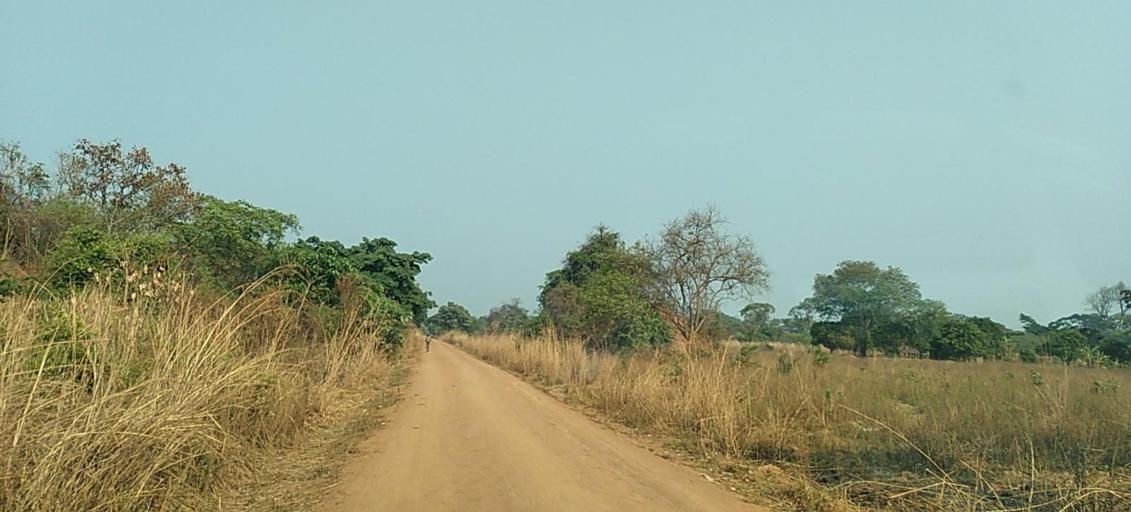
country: ZM
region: Copperbelt
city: Chingola
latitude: -12.8565
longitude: 27.5619
